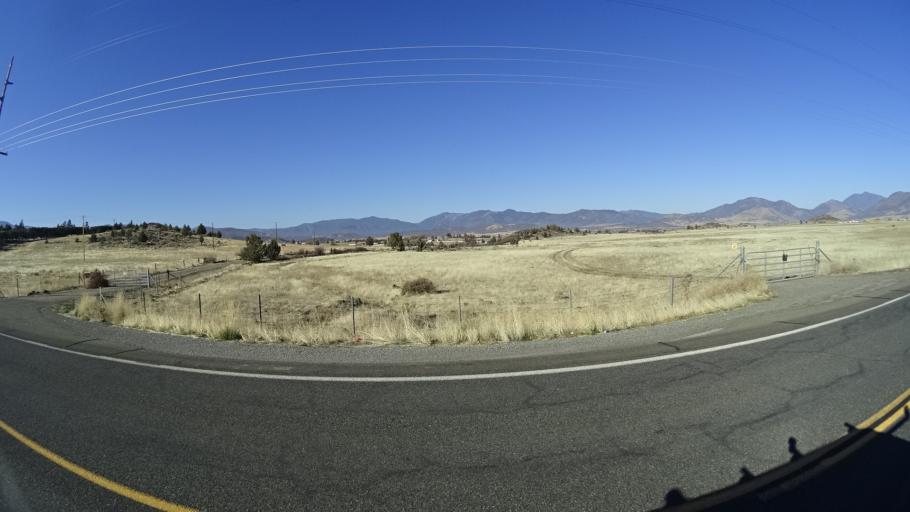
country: US
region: California
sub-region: Siskiyou County
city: Montague
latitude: 41.7145
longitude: -122.5362
